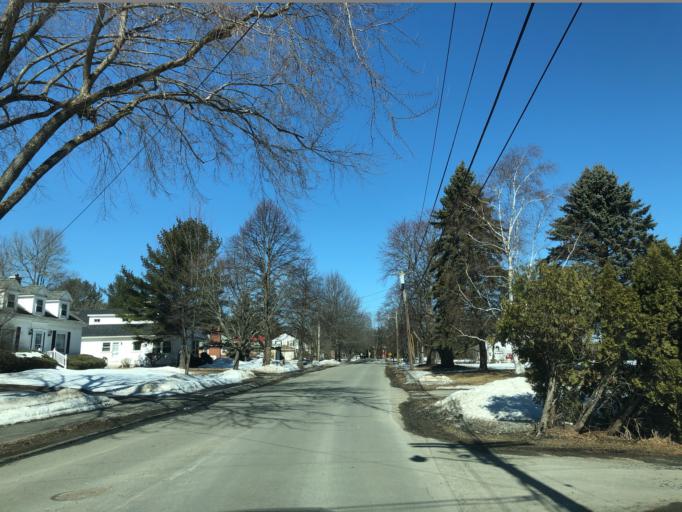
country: US
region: Maine
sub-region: Penobscot County
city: Brewer
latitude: 44.8141
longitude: -68.7532
